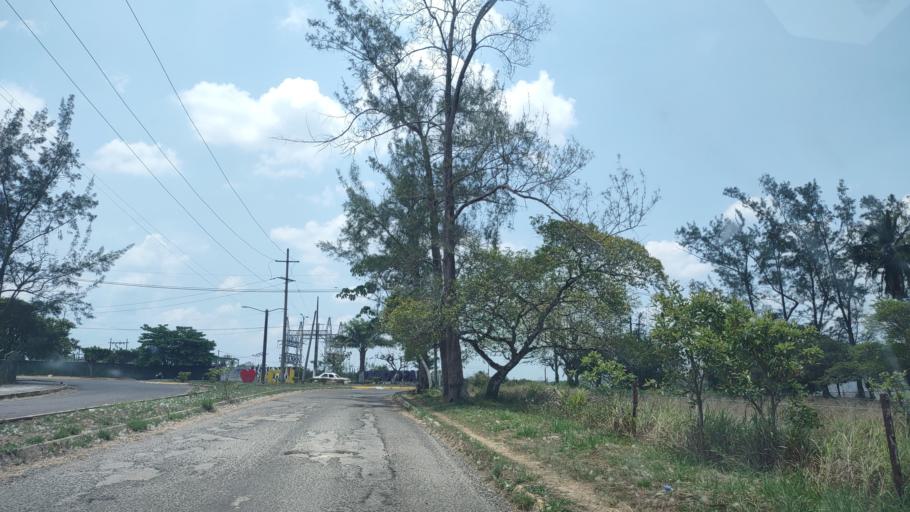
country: MX
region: Veracruz
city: Las Choapas
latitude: 17.9303
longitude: -94.0959
